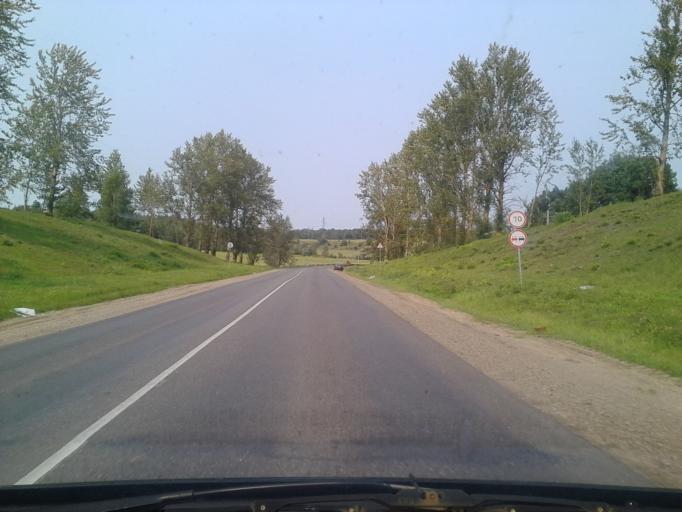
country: BY
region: Minsk
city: Hatava
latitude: 53.7983
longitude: 27.6462
